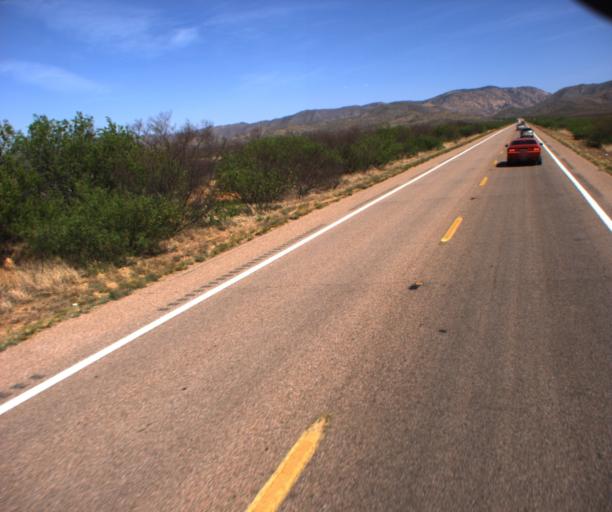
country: US
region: Arizona
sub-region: Cochise County
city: Bisbee
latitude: 31.5343
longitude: -110.0625
